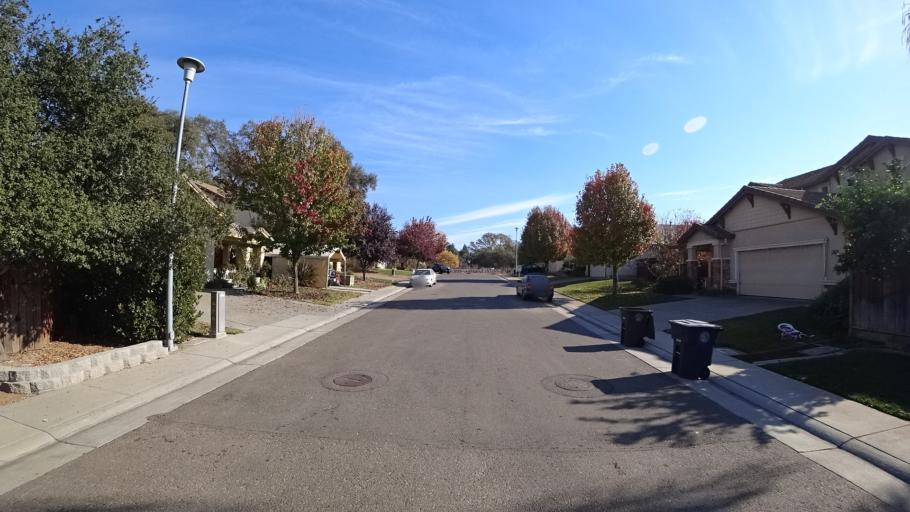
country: US
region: California
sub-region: Sacramento County
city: Citrus Heights
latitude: 38.6845
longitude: -121.2947
